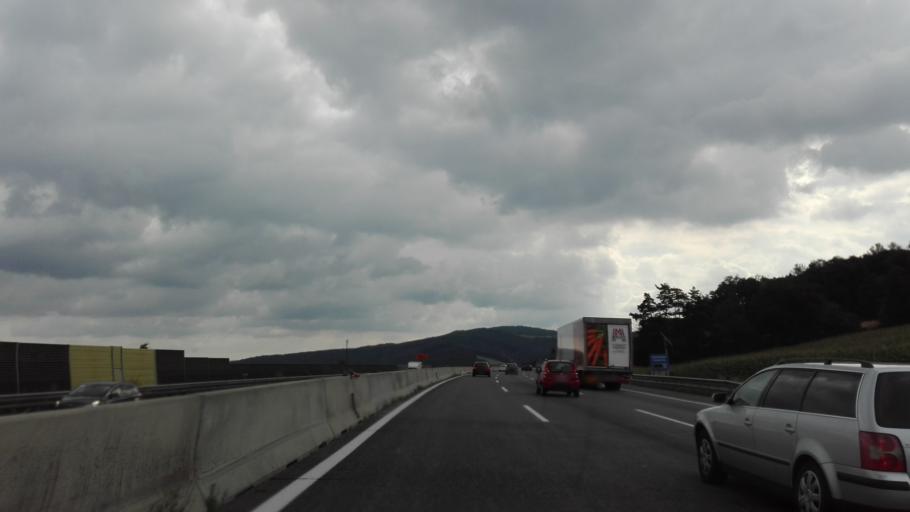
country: AT
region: Lower Austria
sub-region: Politischer Bezirk Sankt Polten
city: Neulengbach
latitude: 48.1745
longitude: 15.8640
